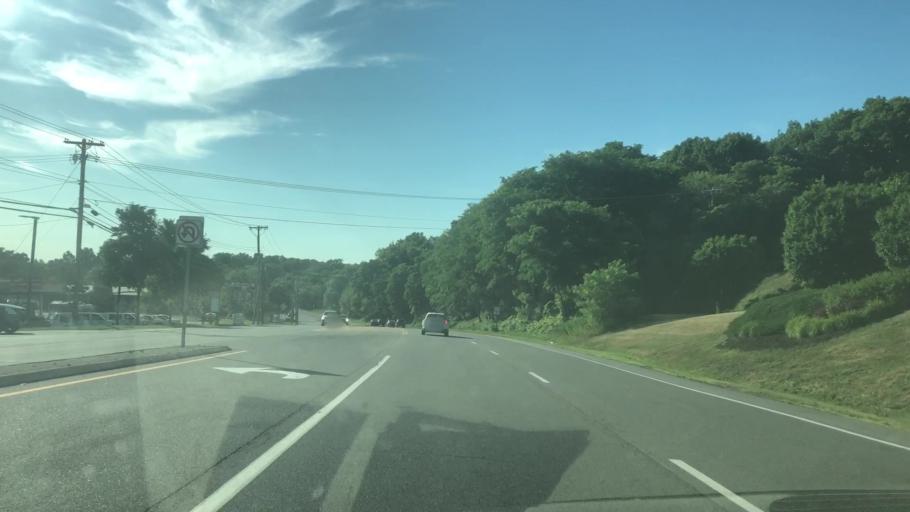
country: US
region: New York
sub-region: Ontario County
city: Victor
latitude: 43.0334
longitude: -77.4429
